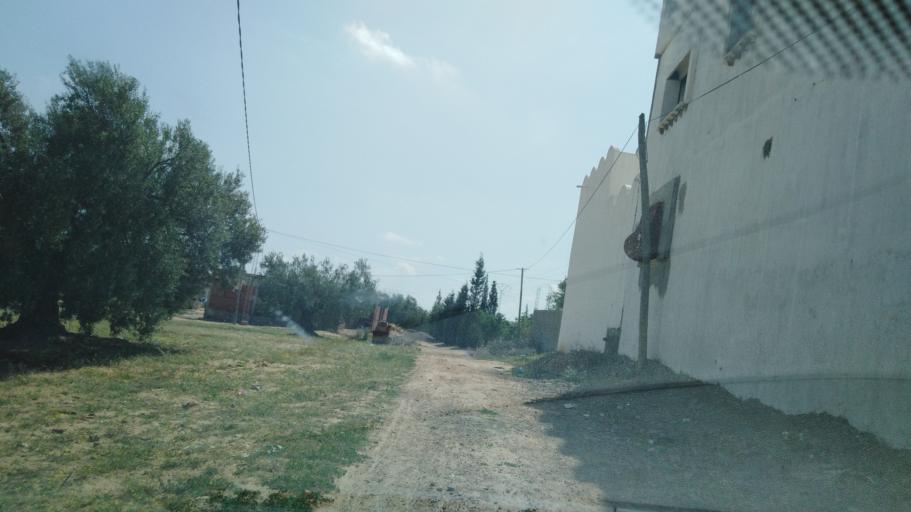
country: TN
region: Safaqis
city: Sfax
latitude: 34.7299
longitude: 10.5637
